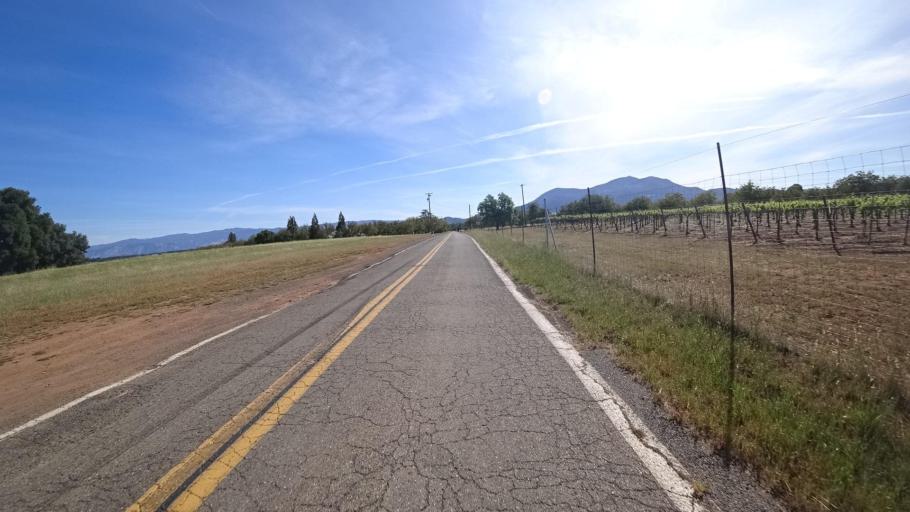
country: US
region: California
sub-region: Lake County
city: Kelseyville
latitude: 38.9663
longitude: -122.8725
